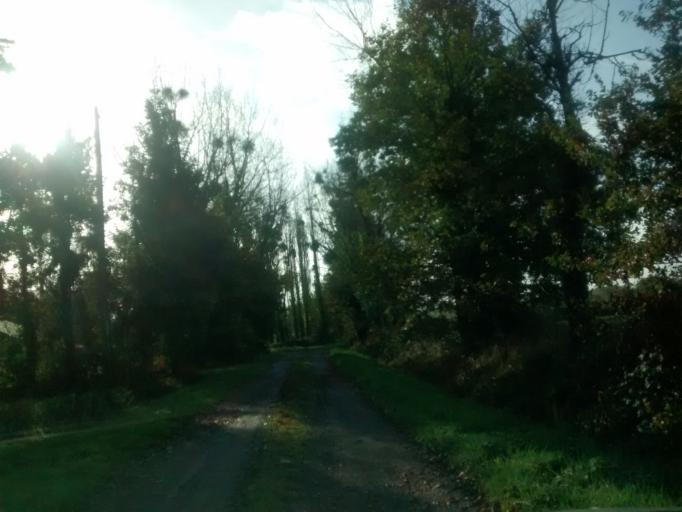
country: FR
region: Brittany
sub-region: Departement d'Ille-et-Vilaine
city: Cesson-Sevigne
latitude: 48.1030
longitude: -1.5909
